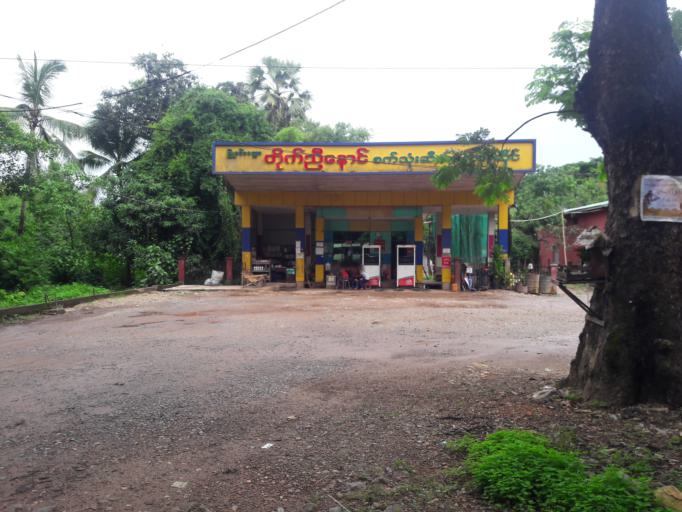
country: MM
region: Bago
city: Nyaunglebin
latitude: 17.7786
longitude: 96.6517
